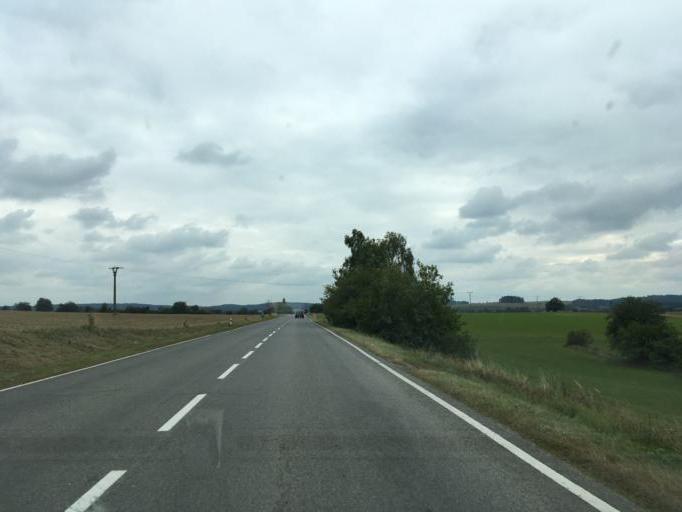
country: CZ
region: Vysocina
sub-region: Okres Pelhrimov
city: Zeliv
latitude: 49.5212
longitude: 15.1726
